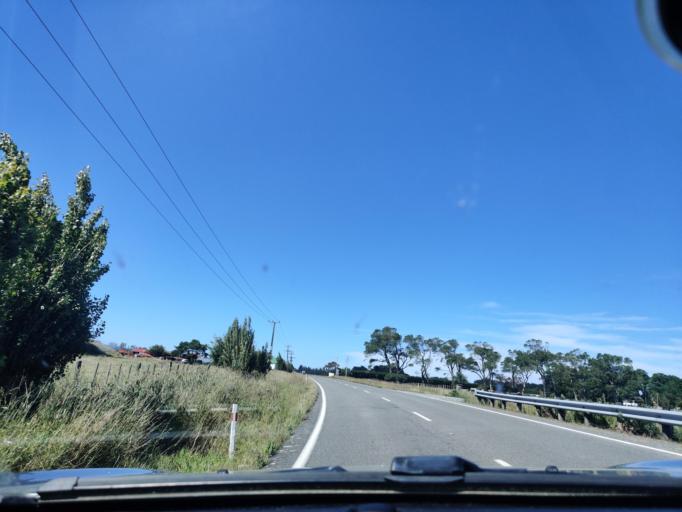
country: NZ
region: Wellington
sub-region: Upper Hutt City
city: Upper Hutt
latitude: -41.3291
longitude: 175.2115
